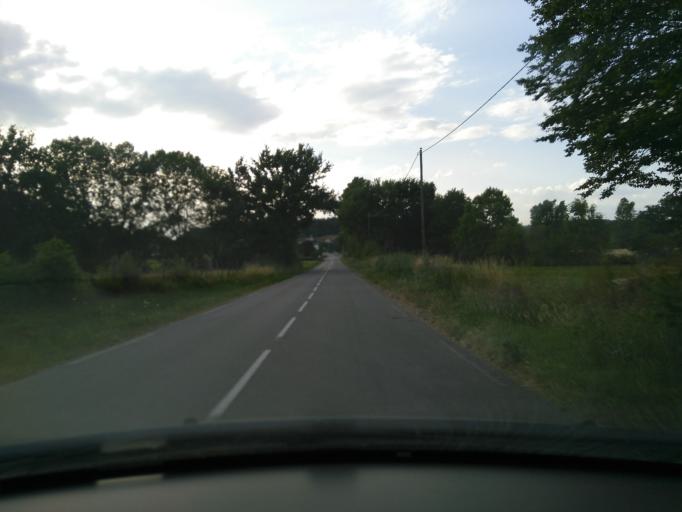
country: FR
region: Rhone-Alpes
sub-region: Departement de l'Isere
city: Beaurepaire
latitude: 45.4007
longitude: 5.1323
